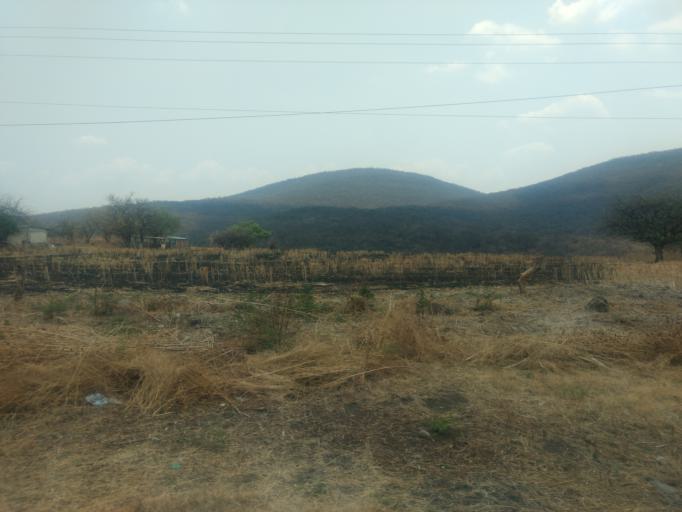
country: MX
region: Morelos
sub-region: Mazatepec
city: Cuauchichinola
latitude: 18.6574
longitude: -99.4124
